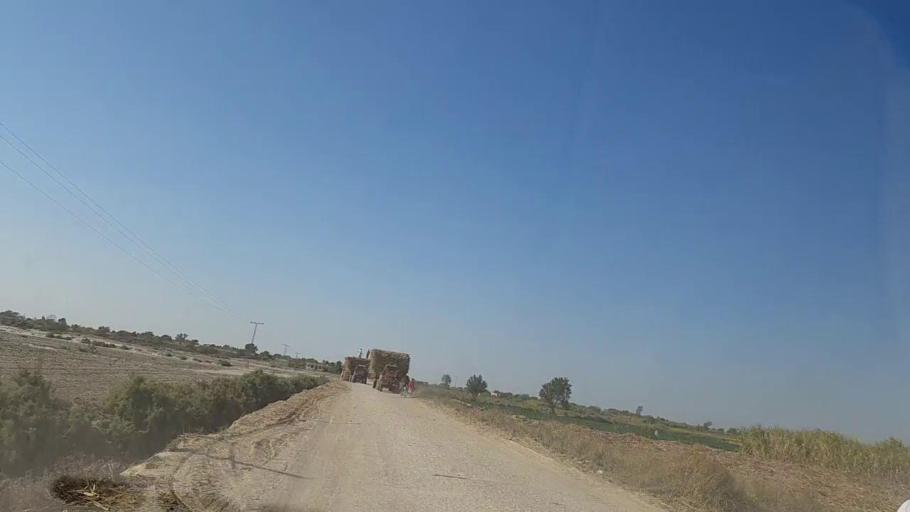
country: PK
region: Sindh
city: Digri
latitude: 25.1741
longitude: 69.0154
